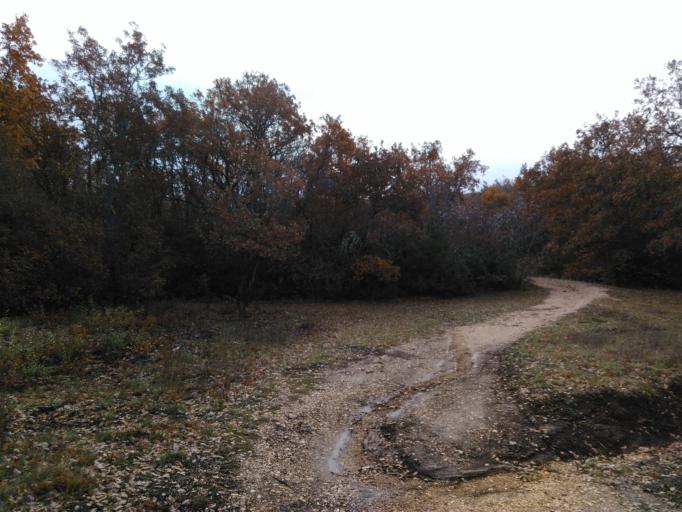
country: FR
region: Provence-Alpes-Cote d'Azur
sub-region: Departement du Vaucluse
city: Villes-sur-Auzon
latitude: 43.9831
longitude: 5.2244
